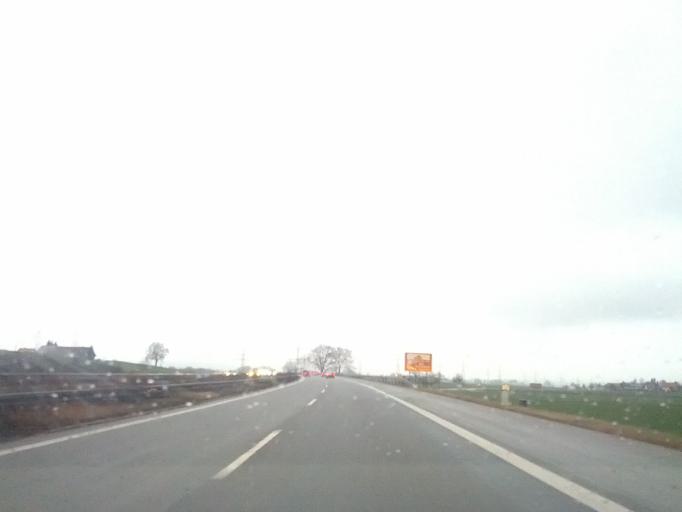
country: DE
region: Bavaria
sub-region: Swabia
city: Wolfertschwenden
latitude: 47.8621
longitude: 10.2747
